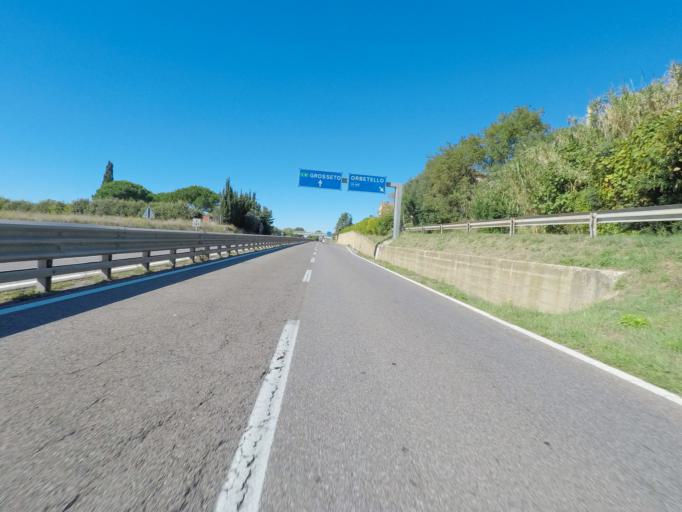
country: IT
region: Tuscany
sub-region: Provincia di Grosseto
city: Orbetello Scalo
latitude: 42.4447
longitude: 11.2602
